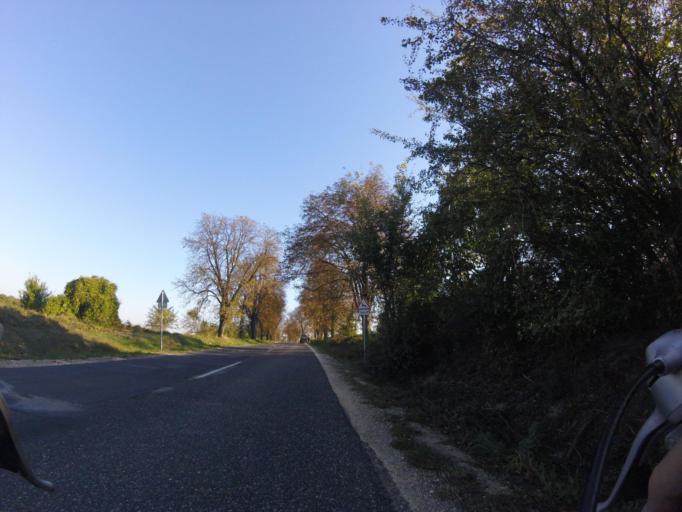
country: HU
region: Fejer
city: Etyek
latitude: 47.4760
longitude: 18.7153
